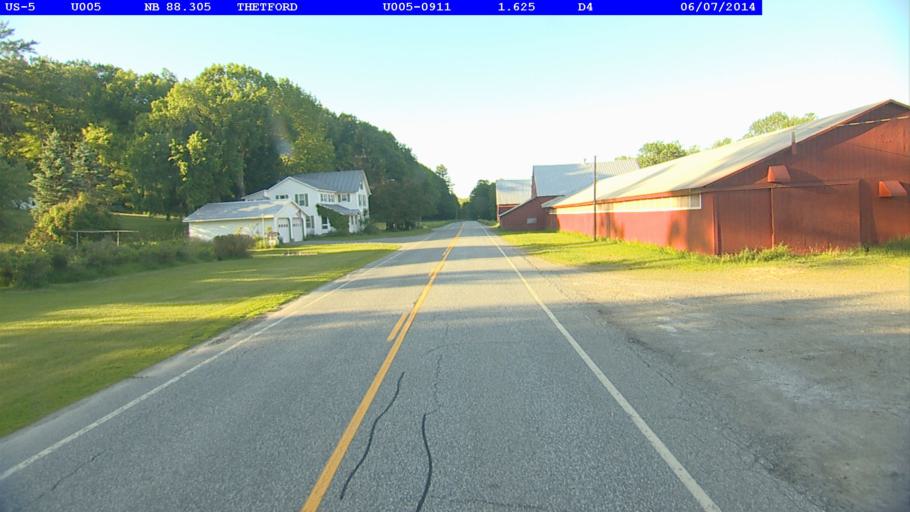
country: US
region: New Hampshire
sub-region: Grafton County
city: Lyme
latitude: 43.7931
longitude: -72.1982
